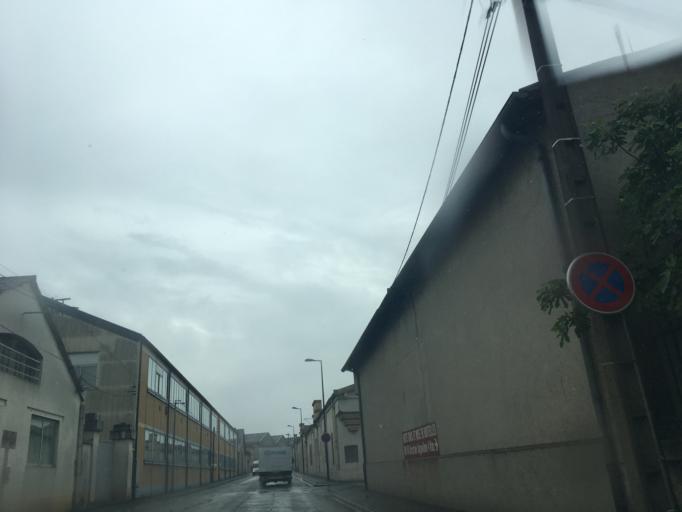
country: FR
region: Poitou-Charentes
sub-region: Departement de la Charente
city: Cognac
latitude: 45.6882
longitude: -0.3193
